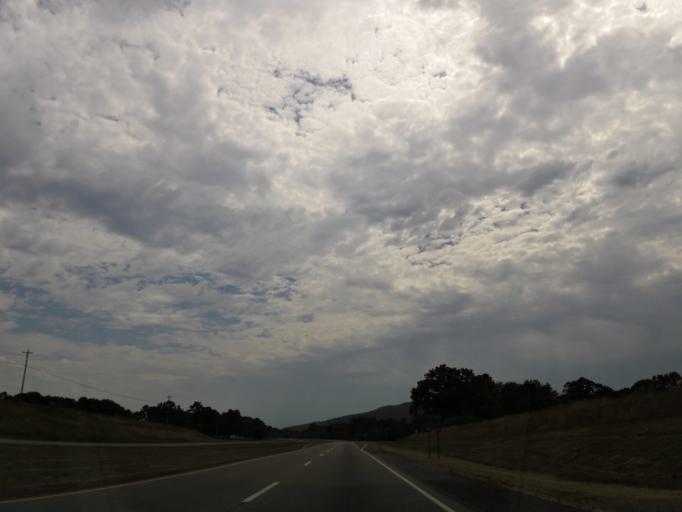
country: US
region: Alabama
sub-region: Jackson County
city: Stevenson
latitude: 34.9044
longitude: -85.8030
